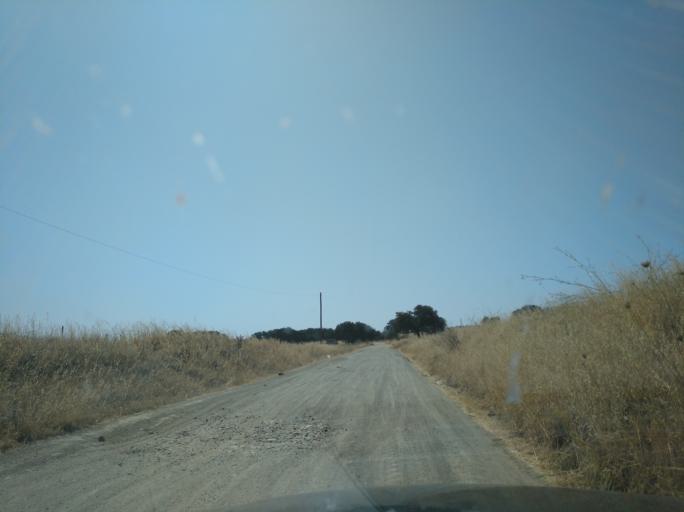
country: PT
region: Portalegre
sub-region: Campo Maior
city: Campo Maior
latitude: 39.0287
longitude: -6.9780
